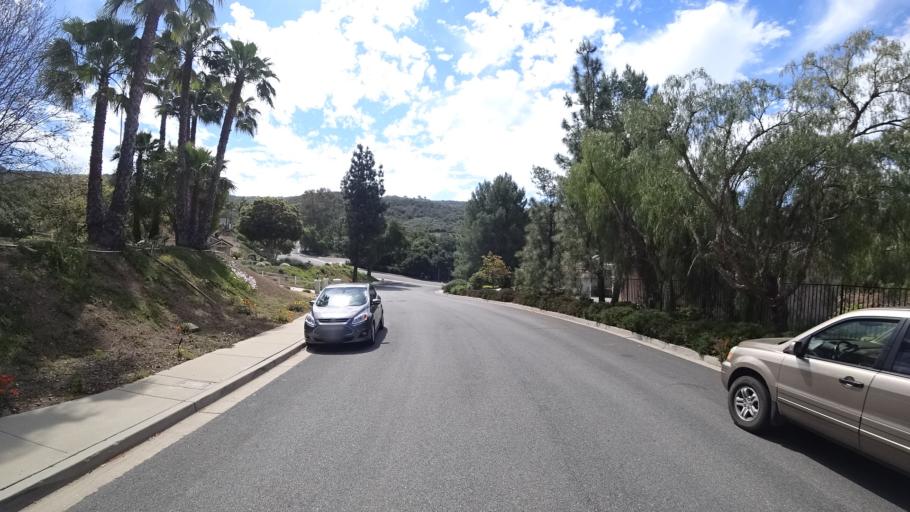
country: US
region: California
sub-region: Ventura County
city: Casa Conejo
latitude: 34.1663
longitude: -118.9368
